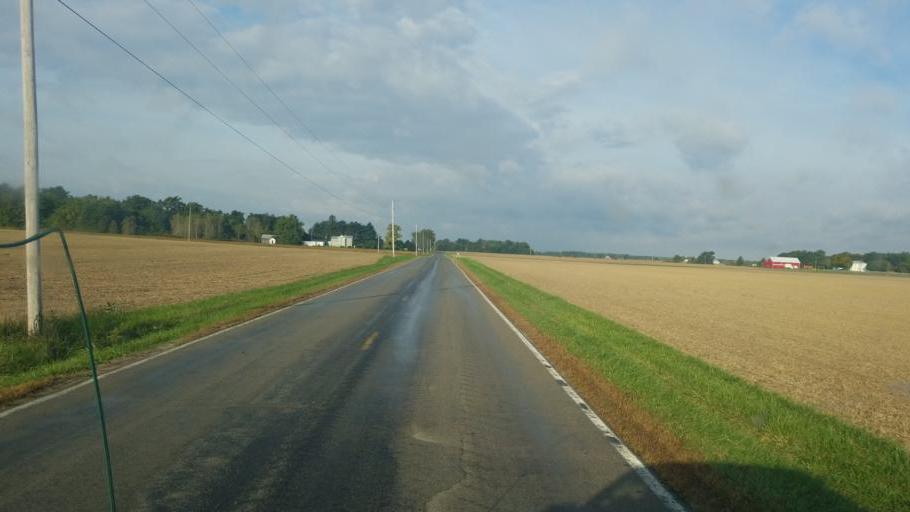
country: US
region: Ohio
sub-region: Wyandot County
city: Upper Sandusky
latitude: 40.8616
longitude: -83.3371
